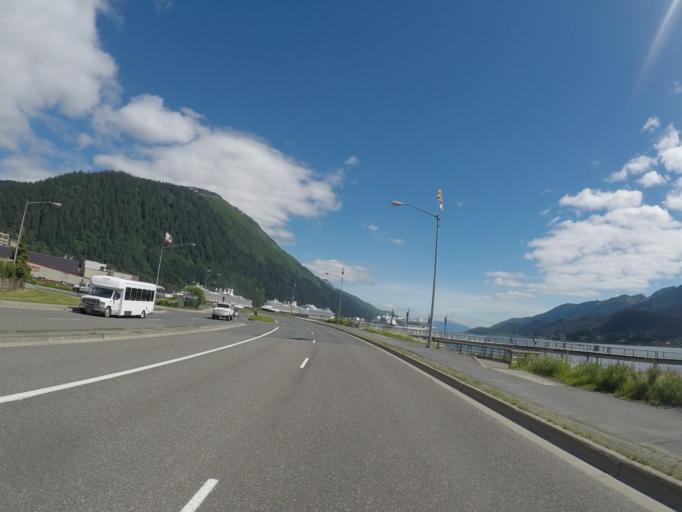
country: US
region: Alaska
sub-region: Juneau City and Borough
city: Juneau
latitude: 58.2993
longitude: -134.4216
